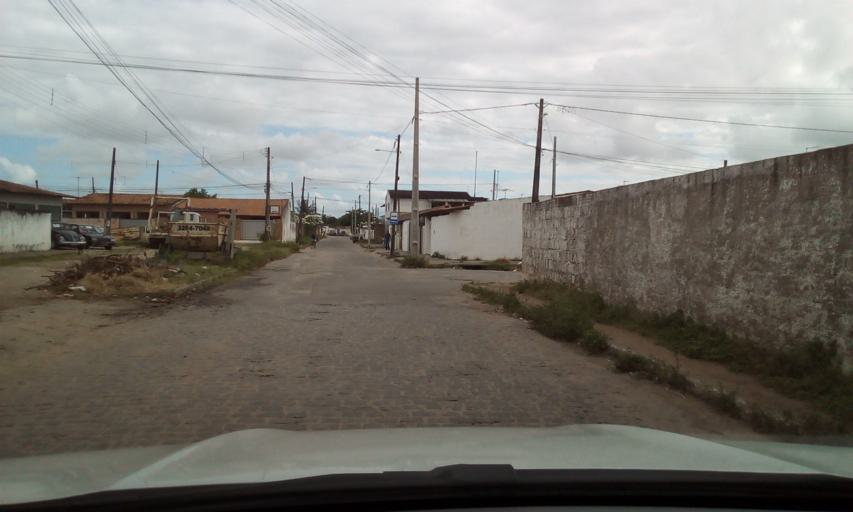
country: BR
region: Paraiba
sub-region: Joao Pessoa
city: Joao Pessoa
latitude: -7.1807
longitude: -34.8774
